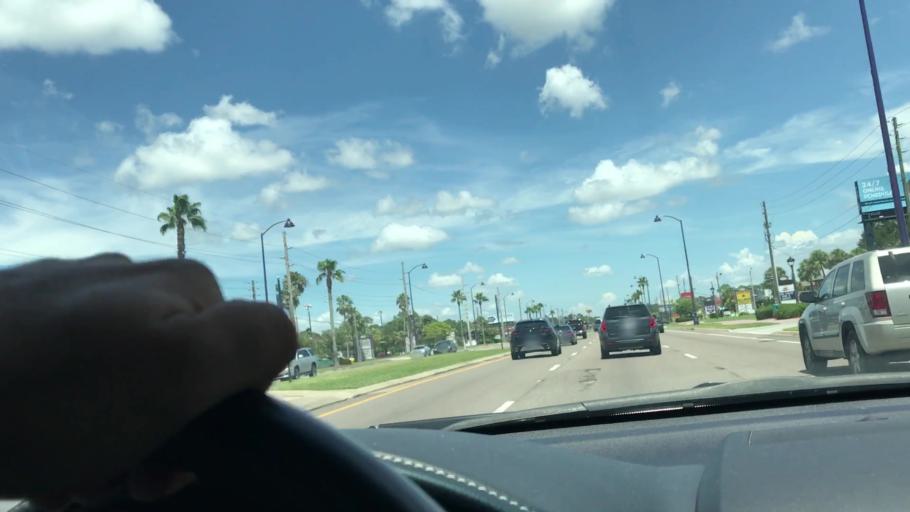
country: US
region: Florida
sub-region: Osceola County
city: Kissimmee
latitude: 28.3130
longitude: -81.4670
